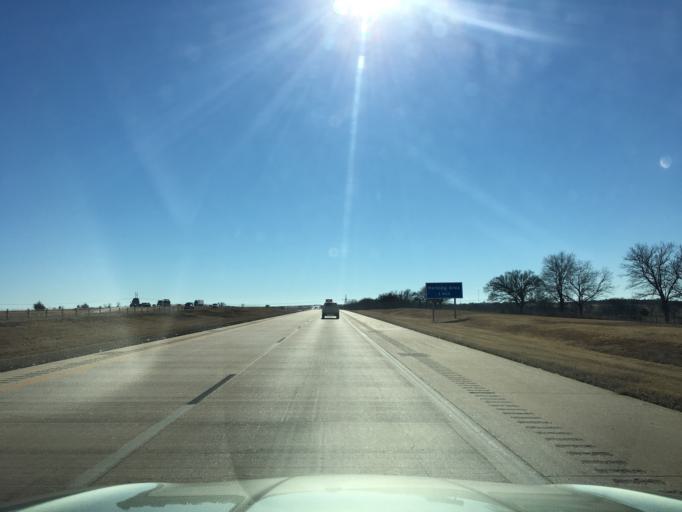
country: US
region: Oklahoma
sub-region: Noble County
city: Perry
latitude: 36.4309
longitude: -97.3271
